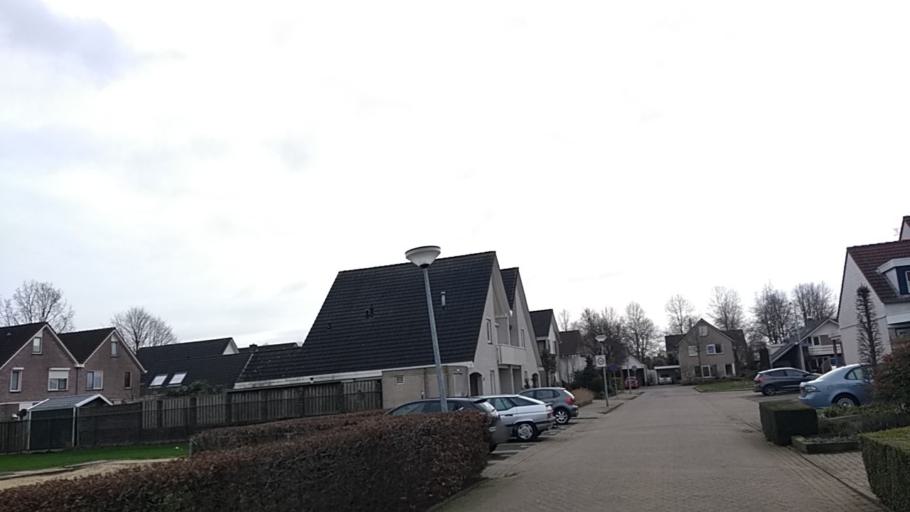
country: NL
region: Overijssel
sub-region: Gemeente Almelo
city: Almelo
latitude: 52.3746
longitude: 6.6852
